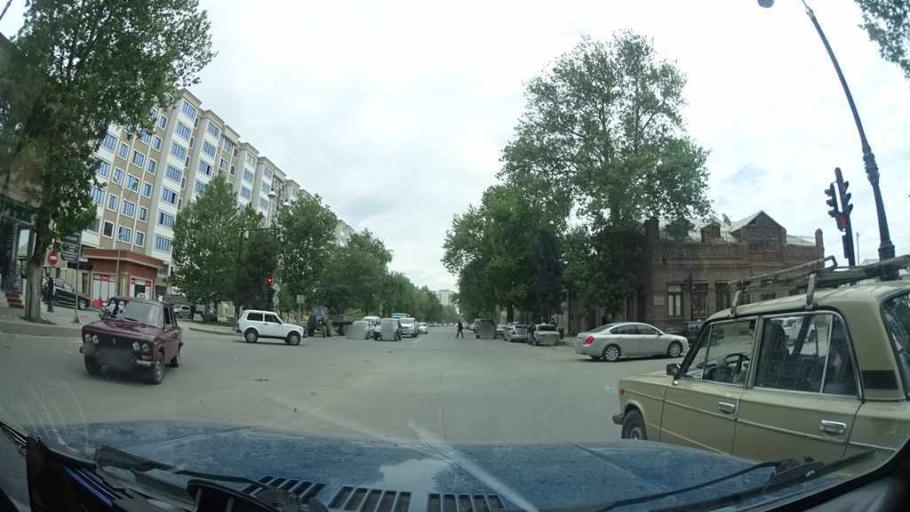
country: AZ
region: Ganja City
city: Ganja
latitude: 40.6830
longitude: 46.3615
